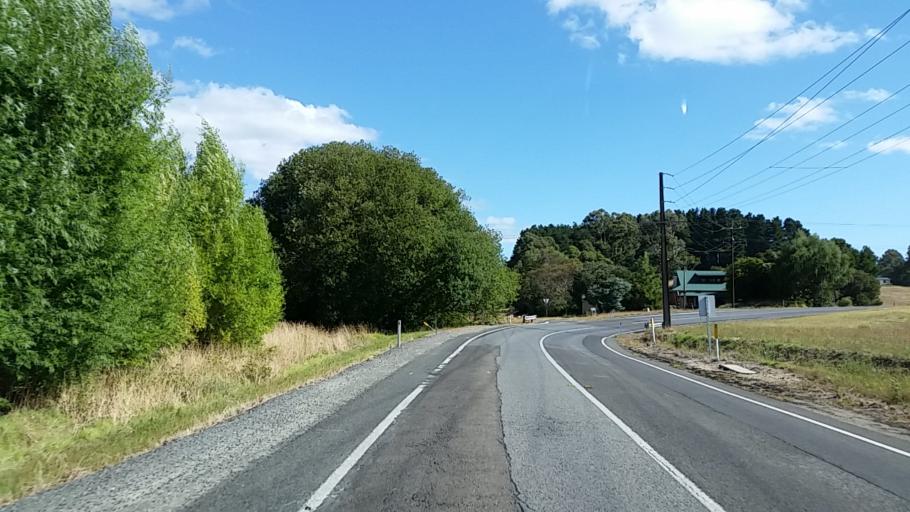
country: AU
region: South Australia
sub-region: Adelaide Hills
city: Bridgewater
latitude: -34.9712
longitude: 138.7330
